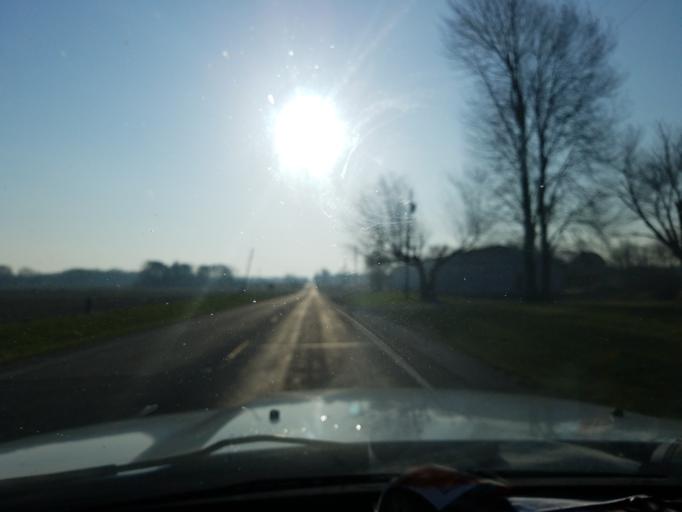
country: US
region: Indiana
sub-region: Vigo County
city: Seelyville
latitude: 39.3887
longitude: -87.1906
